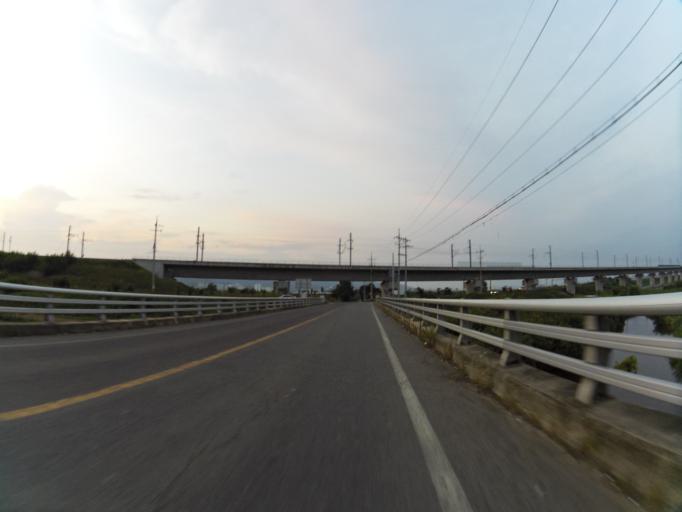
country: KR
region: Gyeongsangbuk-do
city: Gyeongsan-si
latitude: 35.8519
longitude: 128.7478
